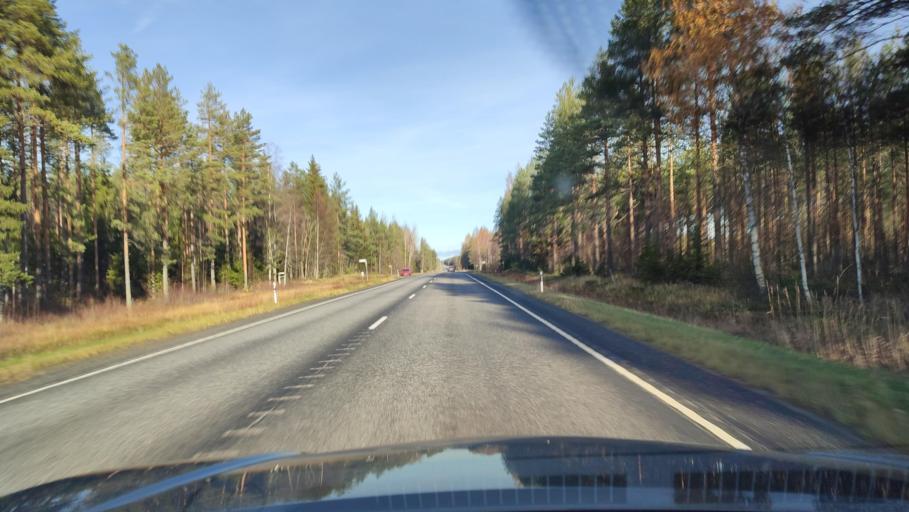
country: FI
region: Ostrobothnia
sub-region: Vaasa
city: Malax
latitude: 62.7998
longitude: 21.6760
